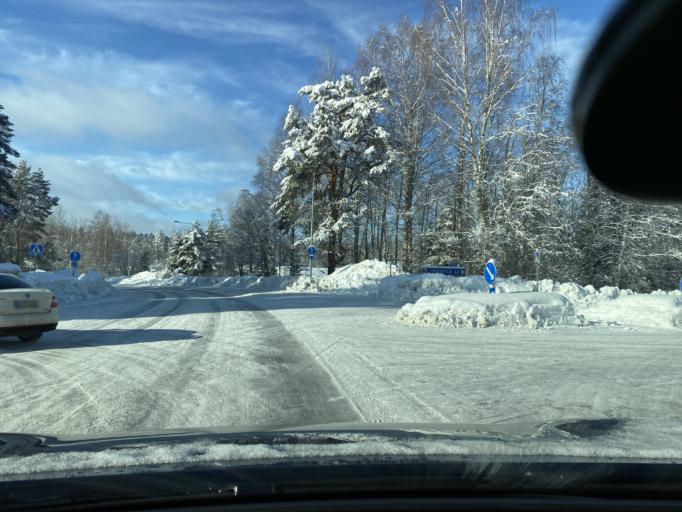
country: FI
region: Southern Savonia
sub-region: Mikkeli
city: Kangasniemi
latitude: 61.9909
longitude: 26.6348
